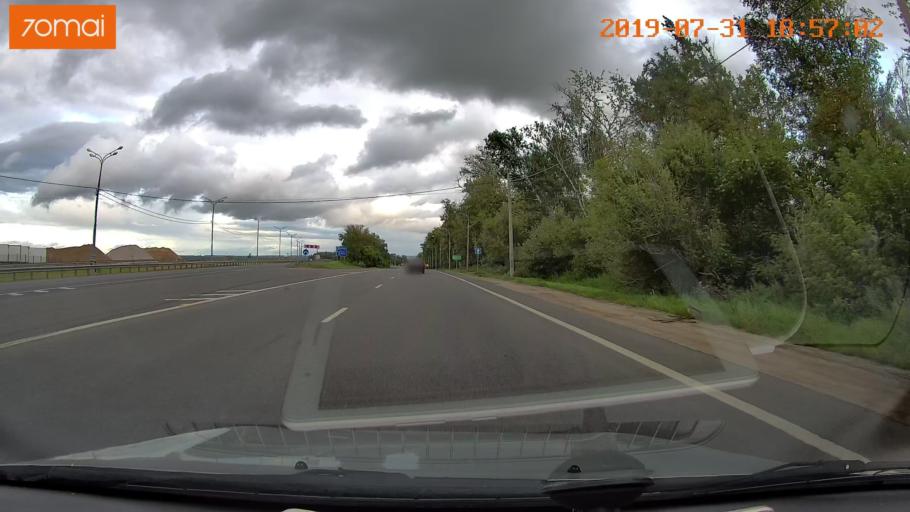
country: RU
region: Moskovskaya
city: Raduzhnyy
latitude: 55.1575
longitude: 38.6865
